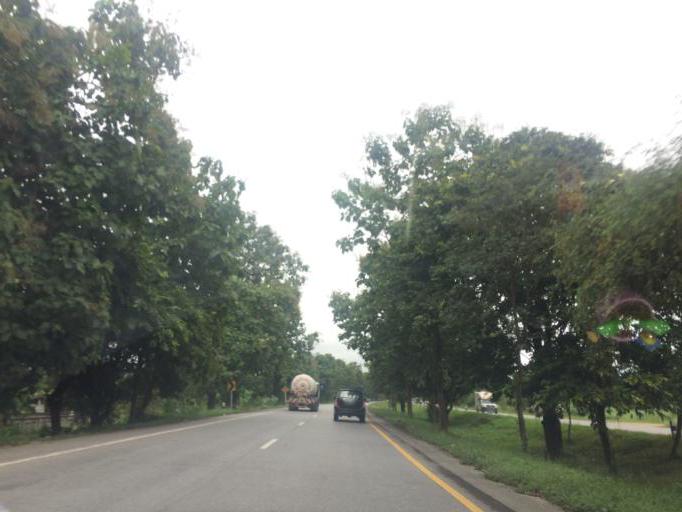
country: TH
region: Chiang Rai
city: Mae Lao
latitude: 19.7808
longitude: 99.7423
